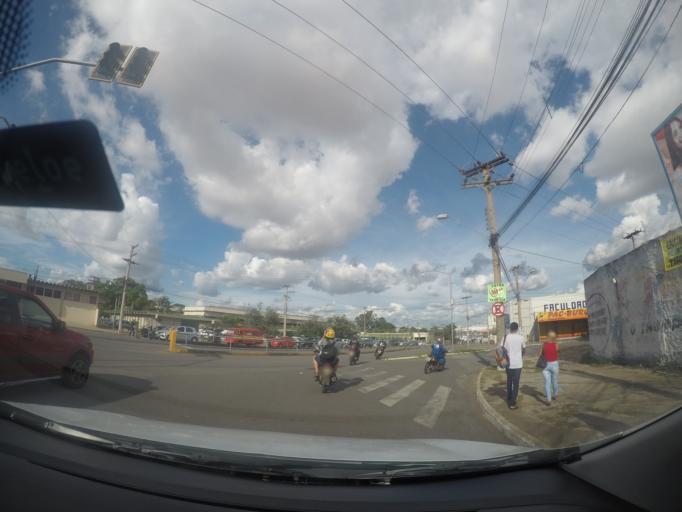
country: BR
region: Goias
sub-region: Goiania
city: Goiania
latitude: -16.6693
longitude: -49.3021
